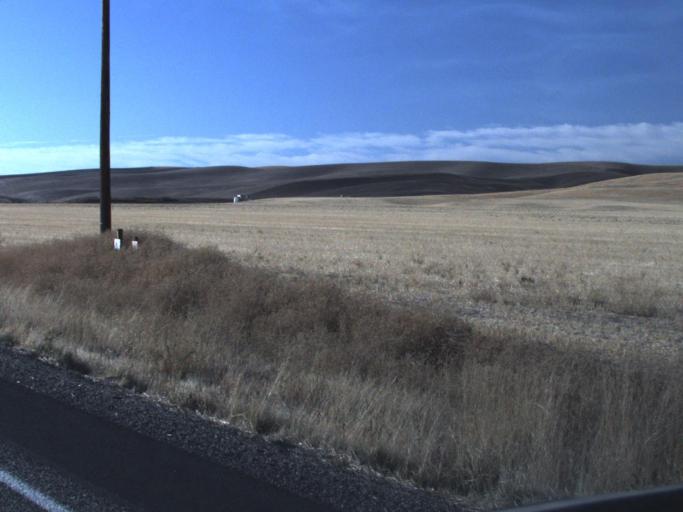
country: US
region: Washington
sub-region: Walla Walla County
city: Waitsburg
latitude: 46.2996
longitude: -118.3787
